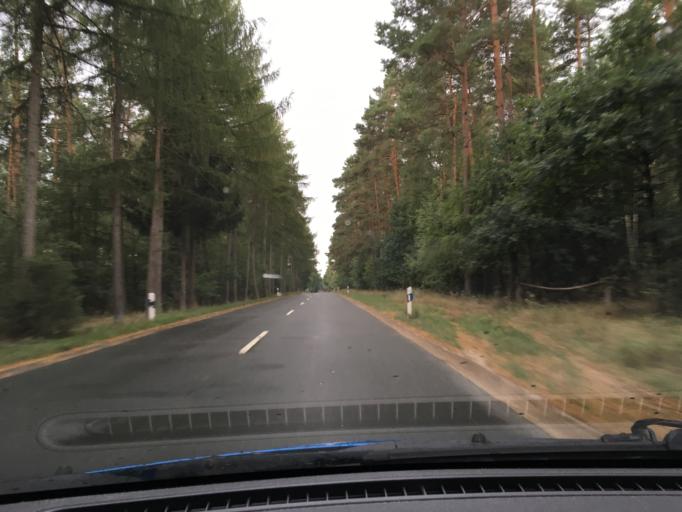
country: DE
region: Lower Saxony
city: Wietzendorf
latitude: 52.8839
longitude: 9.9934
